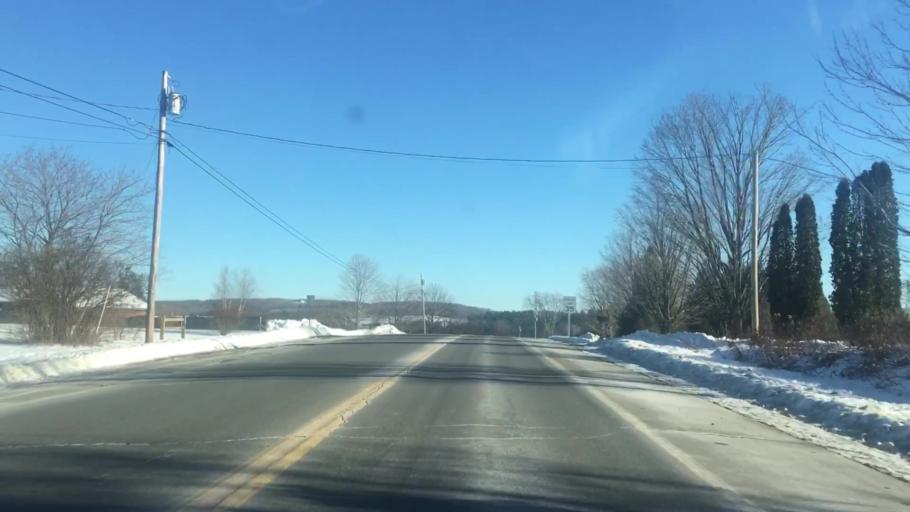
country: US
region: Maine
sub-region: Somerset County
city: Norridgewock
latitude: 44.7229
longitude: -69.8021
